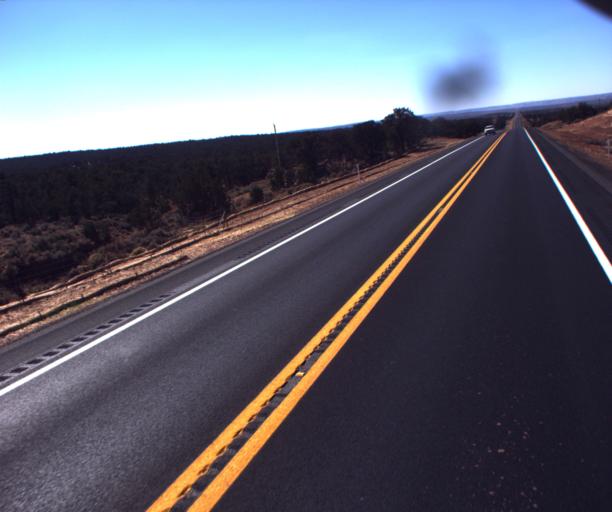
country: US
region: Arizona
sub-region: Apache County
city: Ganado
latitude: 35.7193
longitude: -109.3761
